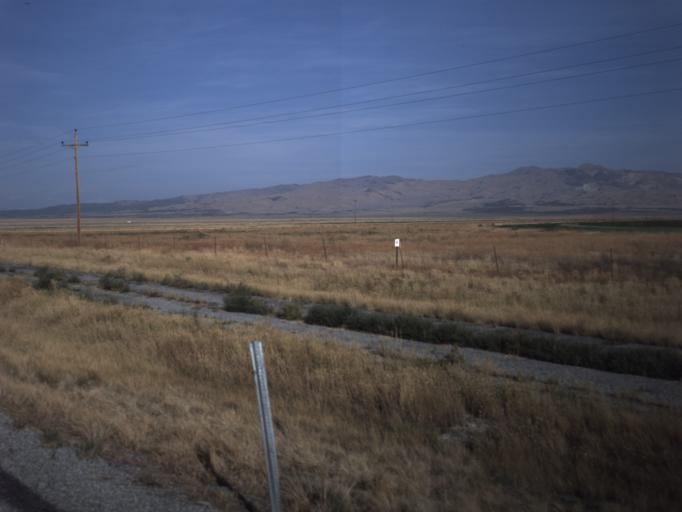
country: US
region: Idaho
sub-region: Oneida County
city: Malad City
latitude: 41.9664
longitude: -112.9376
